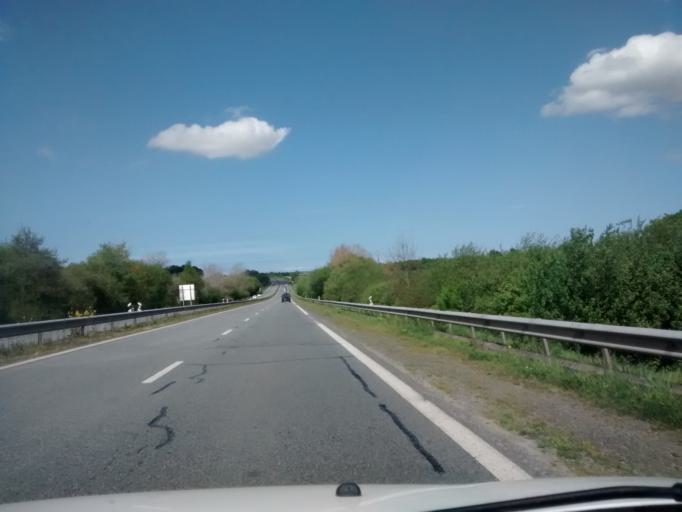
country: FR
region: Brittany
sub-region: Departement des Cotes-d'Armor
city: Saint-Samson-sur-Rance
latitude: 48.4957
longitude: -2.0407
